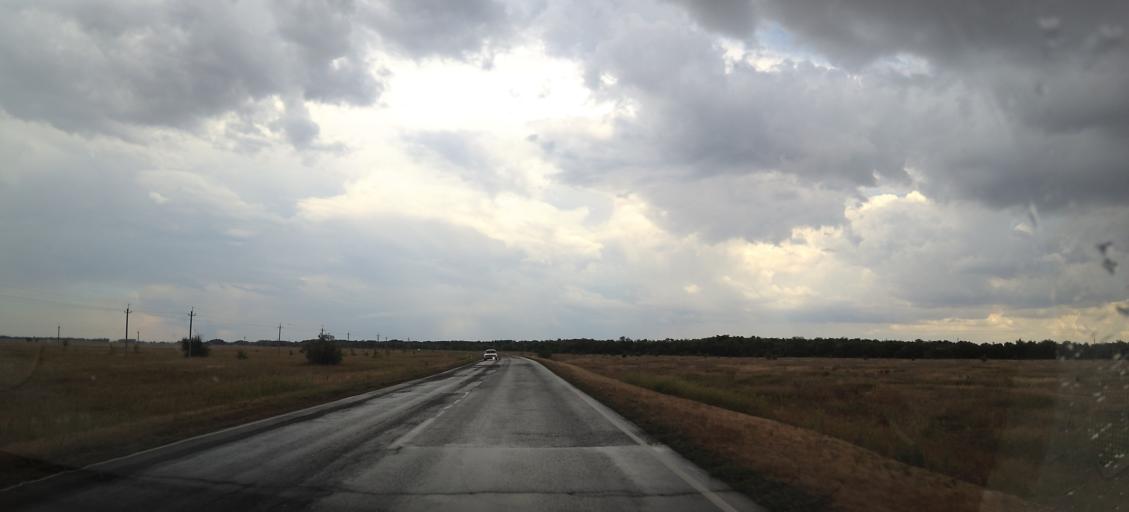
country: RU
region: Rostov
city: Dubovskoye
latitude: 47.2945
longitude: 42.6109
